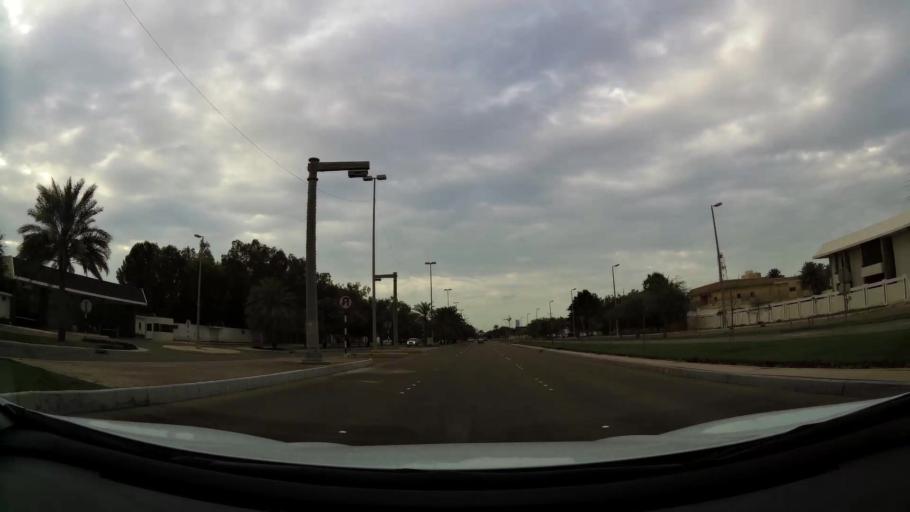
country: AE
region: Abu Dhabi
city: Abu Dhabi
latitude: 24.4328
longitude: 54.3690
